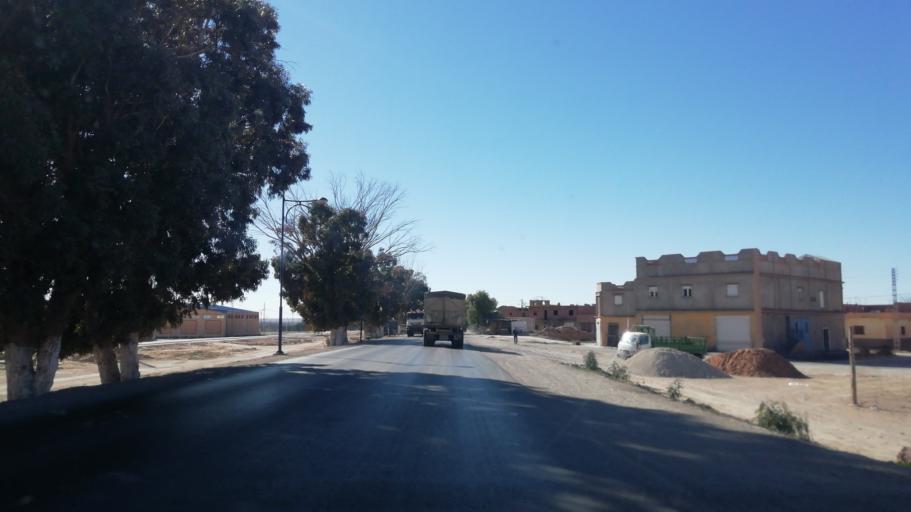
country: DZ
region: Saida
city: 'Ain el Hadjar
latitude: 34.1539
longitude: 0.0701
